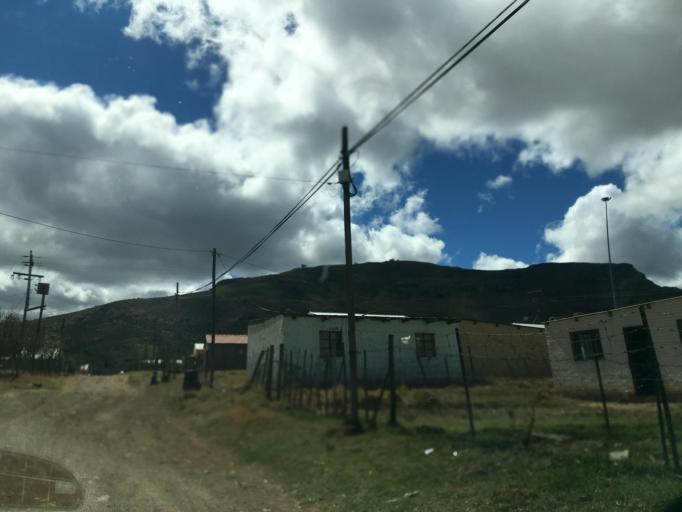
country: ZA
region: Eastern Cape
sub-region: Chris Hani District Municipality
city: Cala
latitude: -31.5319
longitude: 27.7022
